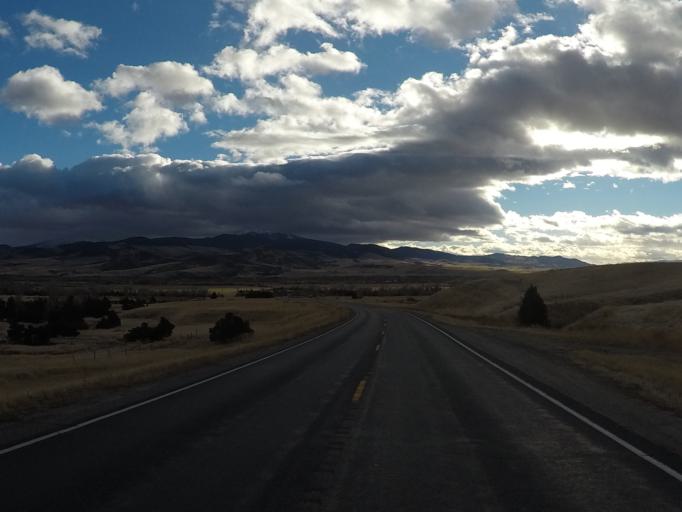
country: US
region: Montana
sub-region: Jefferson County
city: Whitehall
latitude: 45.8784
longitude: -111.9758
